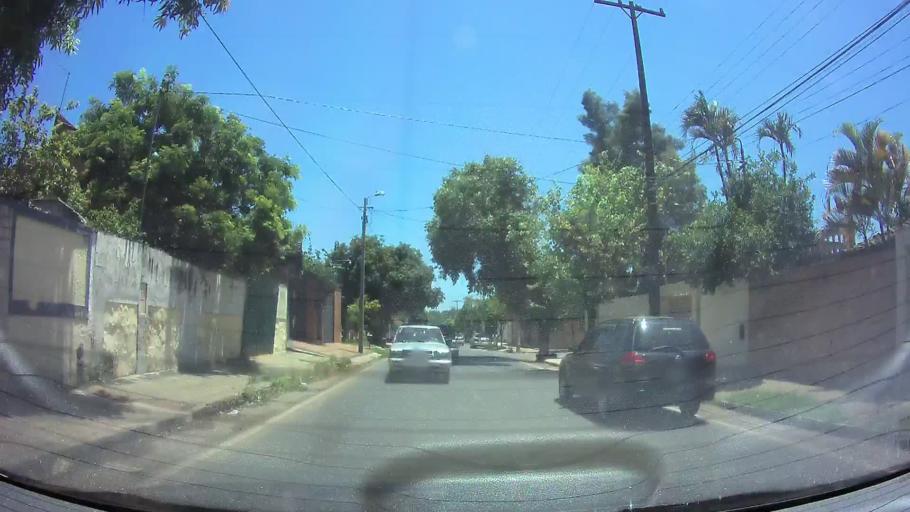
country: PY
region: Central
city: San Lorenzo
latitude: -25.2674
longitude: -57.5059
